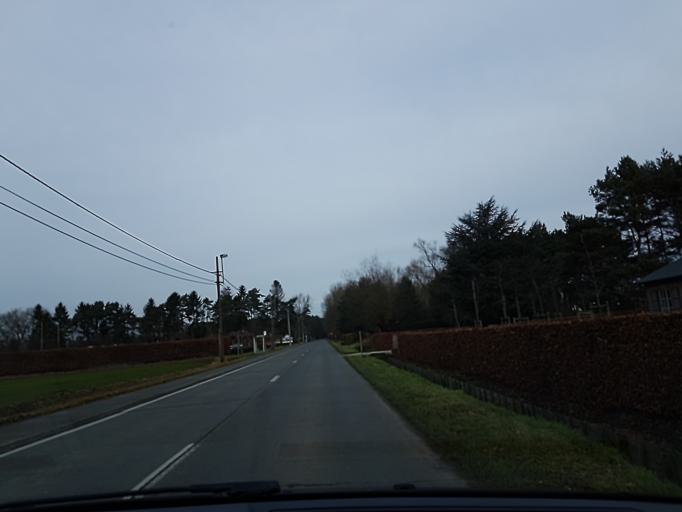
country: BE
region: Flanders
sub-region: Provincie Vlaams-Brabant
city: Keerbergen
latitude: 51.0179
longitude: 4.6012
